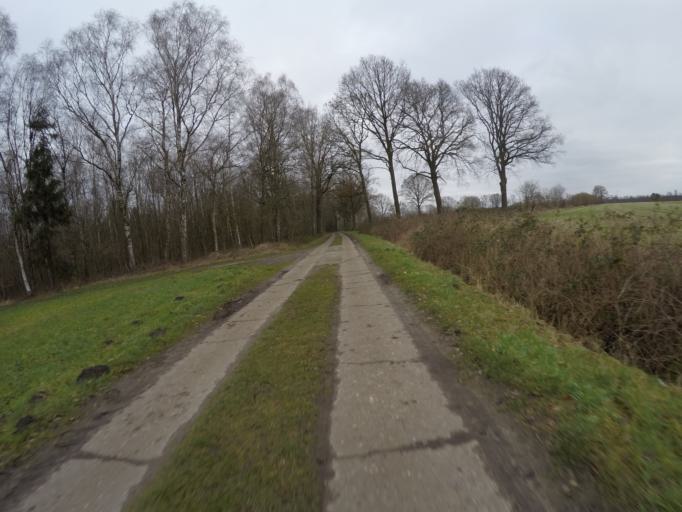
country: DE
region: Schleswig-Holstein
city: Hemdingen
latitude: 53.7804
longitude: 9.8429
